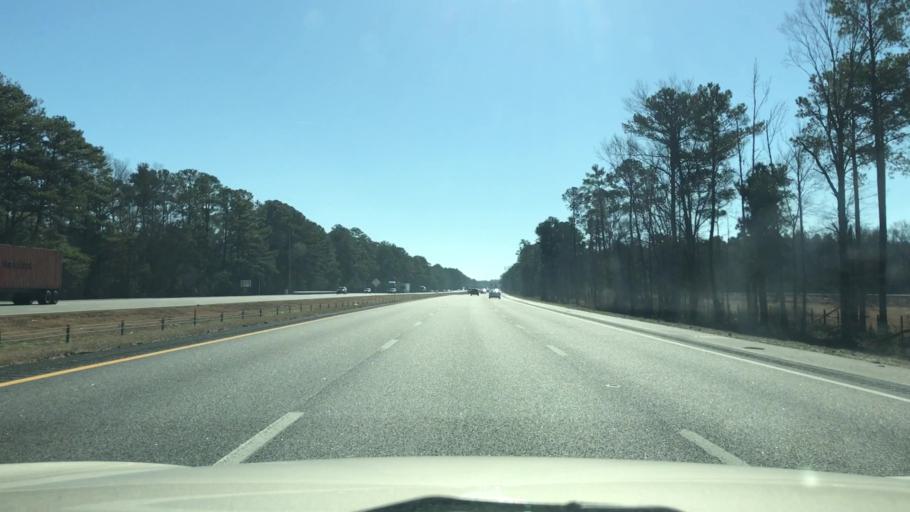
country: US
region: South Carolina
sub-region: Lexington County
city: Pineridge
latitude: 33.9076
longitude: -81.0533
